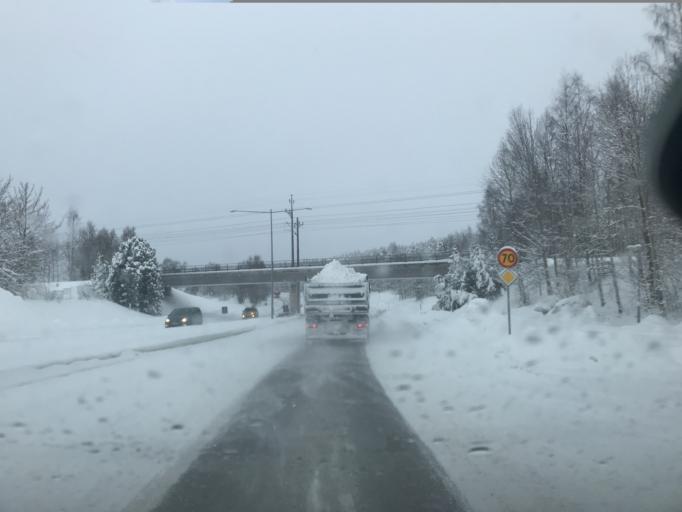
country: SE
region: Norrbotten
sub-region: Lulea Kommun
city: Lulea
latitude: 65.6038
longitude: 22.1372
